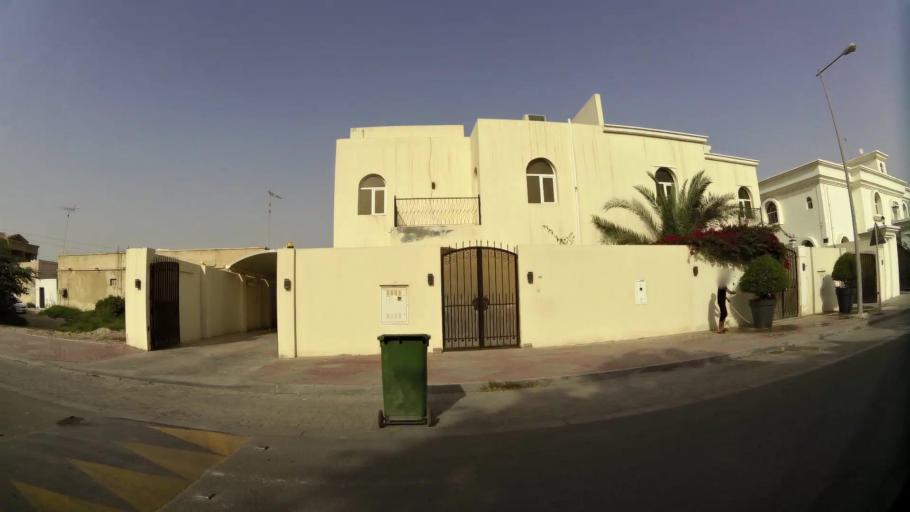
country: QA
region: Baladiyat ar Rayyan
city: Ar Rayyan
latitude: 25.2350
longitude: 51.4437
